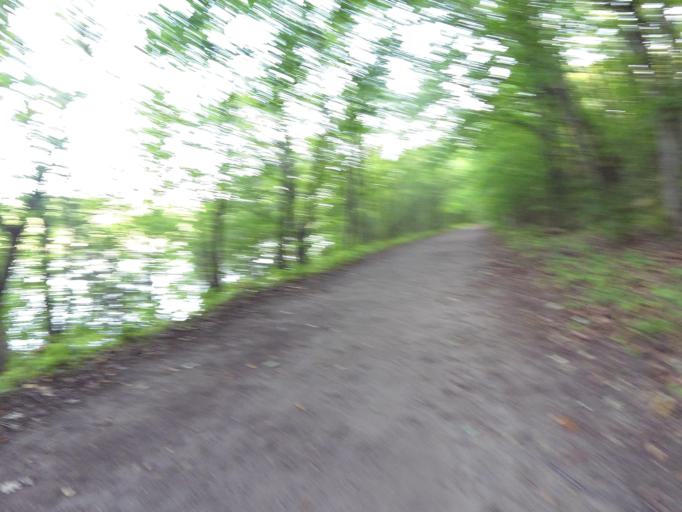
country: US
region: Minnesota
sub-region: Washington County
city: Afton
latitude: 44.8432
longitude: -92.7697
